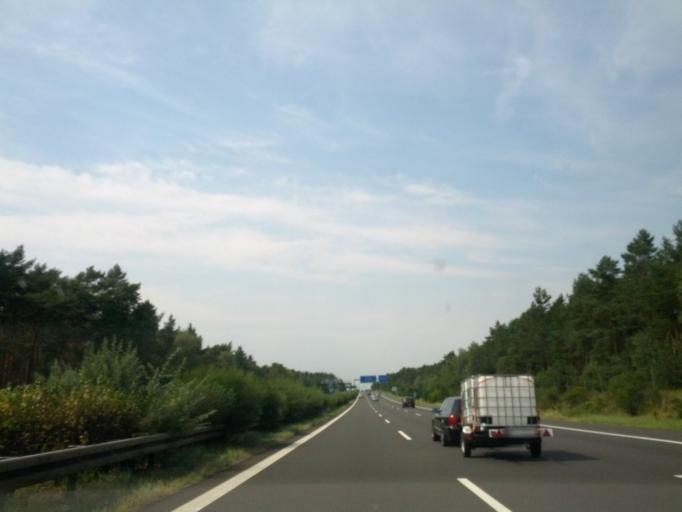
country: DE
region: Brandenburg
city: Fichtenwalde
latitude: 52.3058
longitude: 12.8853
